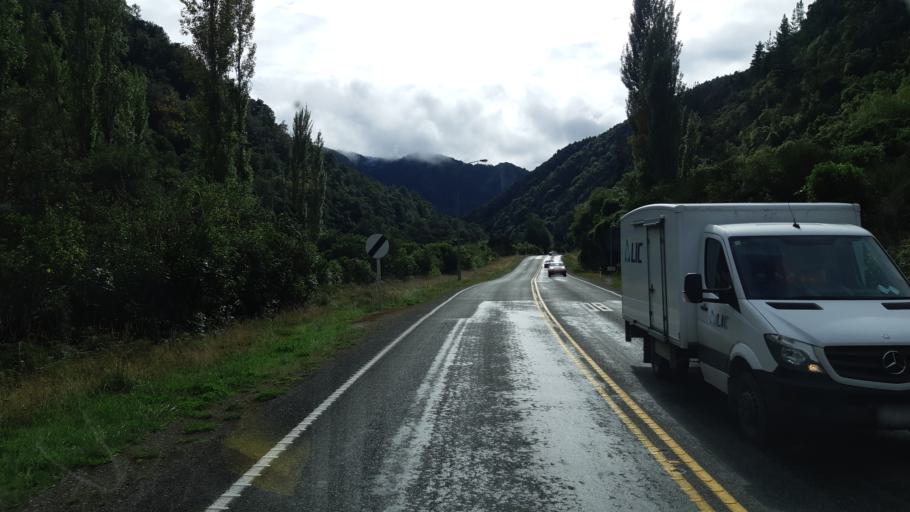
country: NZ
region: West Coast
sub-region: Buller District
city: Westport
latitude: -41.7765
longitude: 172.2205
